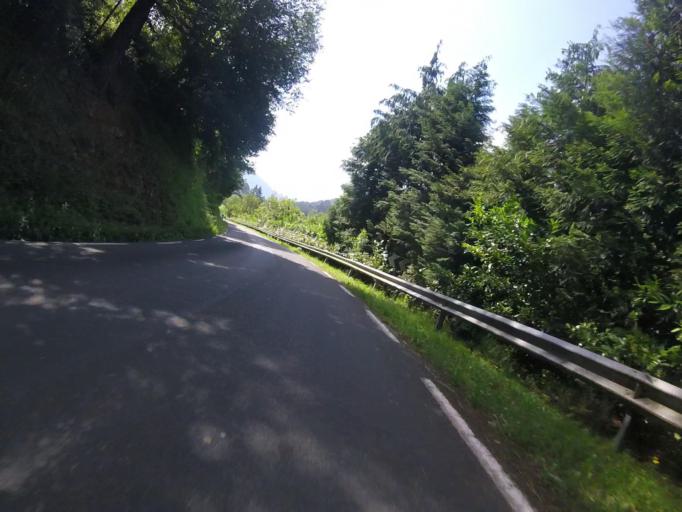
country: ES
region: Basque Country
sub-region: Provincia de Guipuzcoa
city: Alquiza
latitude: 43.1696
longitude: -2.1036
